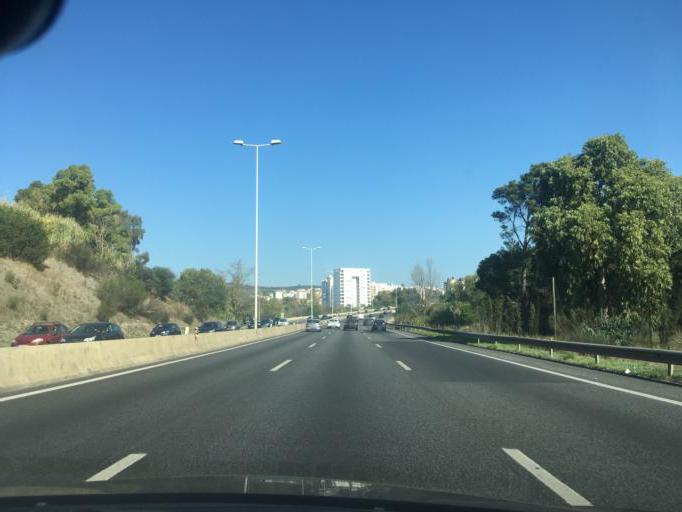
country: PT
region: Lisbon
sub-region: Oeiras
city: Linda-a-Velha
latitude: 38.7170
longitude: -9.2516
